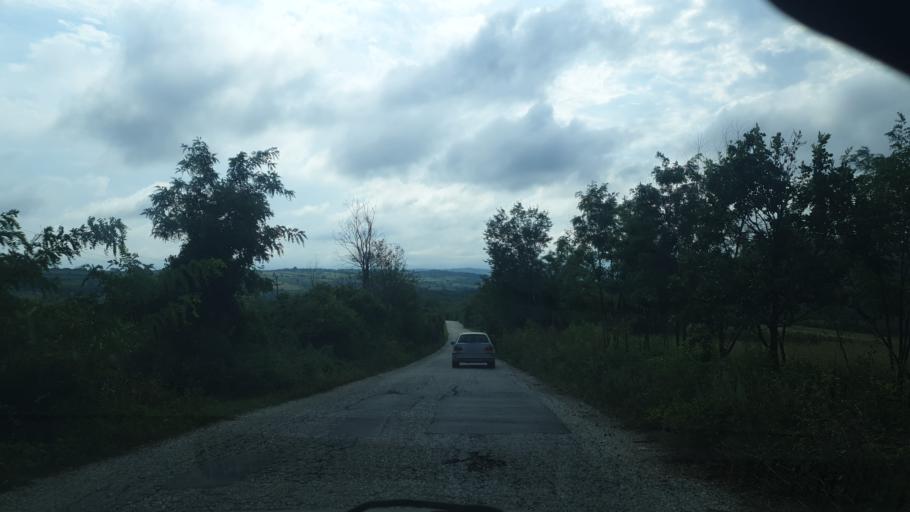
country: RS
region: Central Serbia
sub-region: Sumadijski Okrug
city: Kragujevac
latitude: 44.0967
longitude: 20.7852
